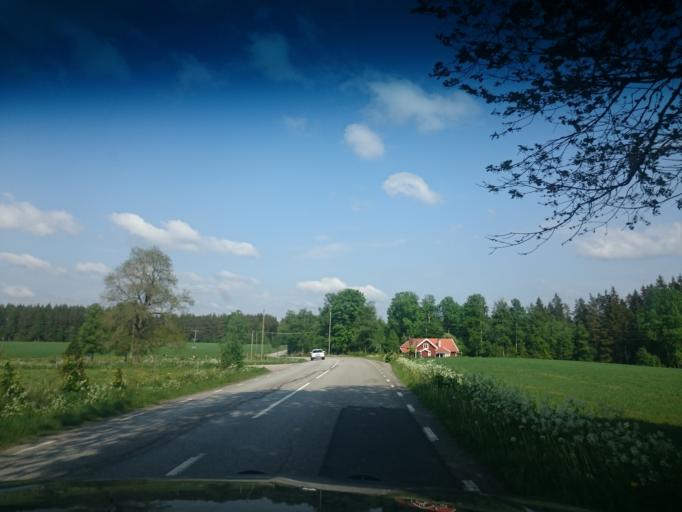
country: SE
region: Joenkoeping
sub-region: Vetlanda Kommun
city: Vetlanda
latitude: 57.3793
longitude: 14.9997
